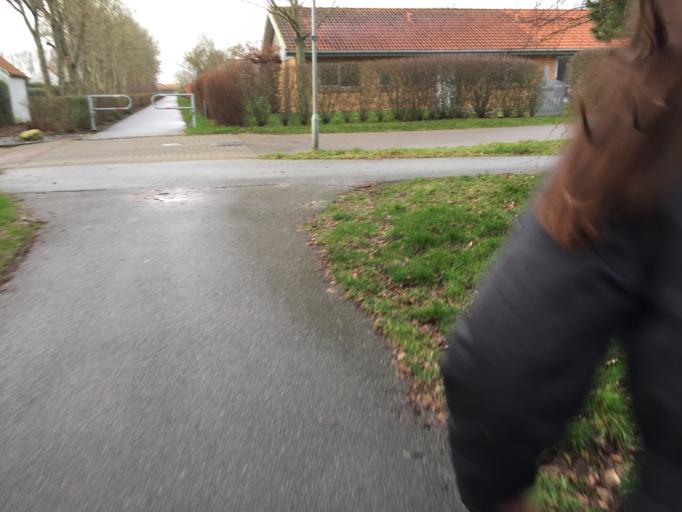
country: DK
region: Central Jutland
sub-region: Ringkobing-Skjern Kommune
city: Ringkobing
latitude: 56.0936
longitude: 8.2702
